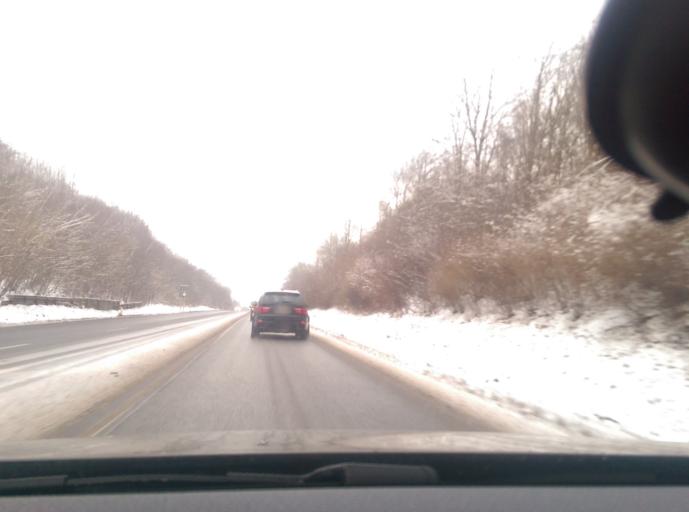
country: DE
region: Hesse
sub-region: Regierungsbezirk Kassel
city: Kaufungen
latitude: 51.2780
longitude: 9.6124
